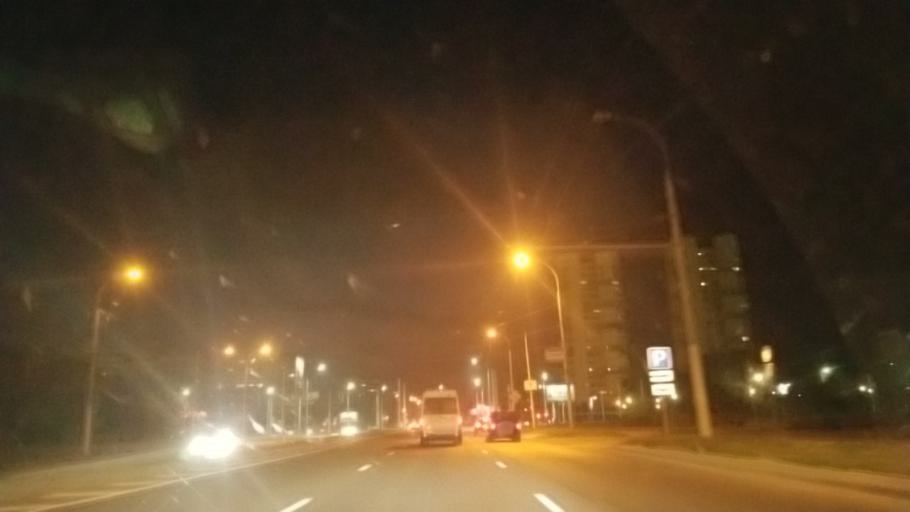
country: BY
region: Brest
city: Brest
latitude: 52.0980
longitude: 23.7649
